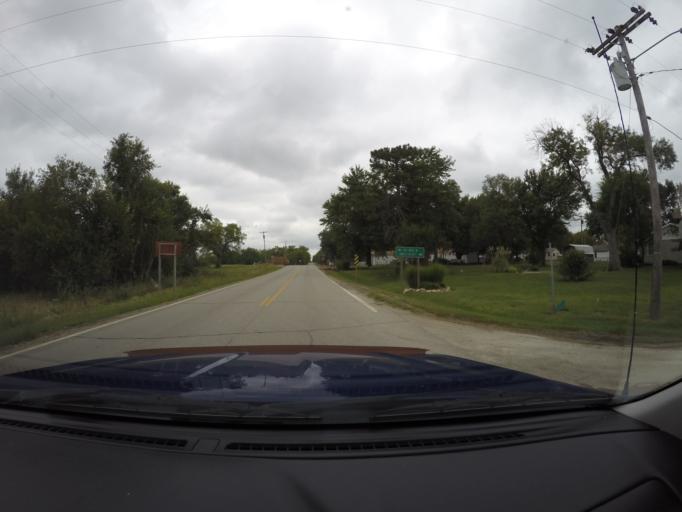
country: US
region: Kansas
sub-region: Morris County
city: Council Grove
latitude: 38.8412
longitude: -96.5925
